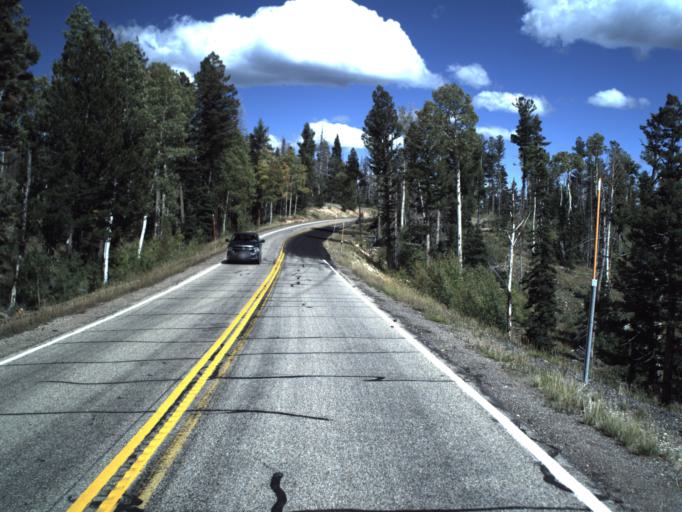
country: US
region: Utah
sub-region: Iron County
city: Parowan
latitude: 37.5272
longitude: -112.7583
